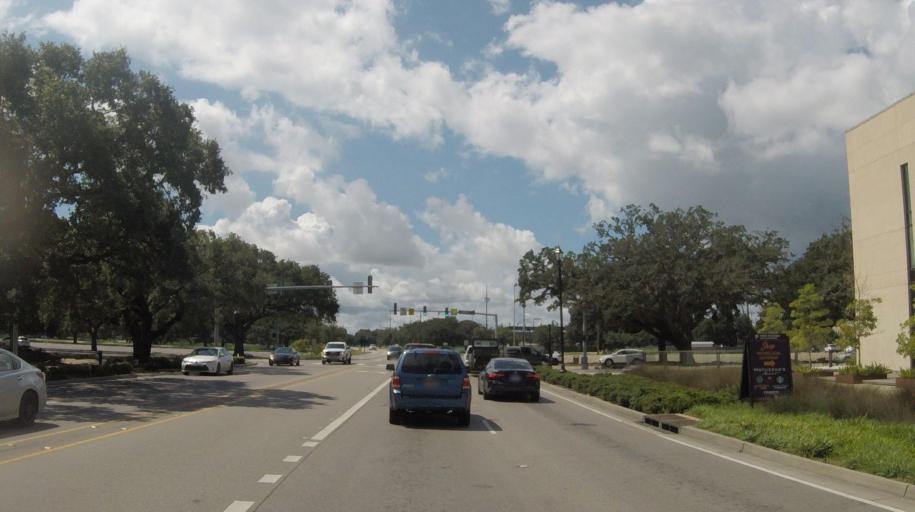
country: US
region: Louisiana
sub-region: West Baton Rouge Parish
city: Port Allen
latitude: 30.4120
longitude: -91.1865
